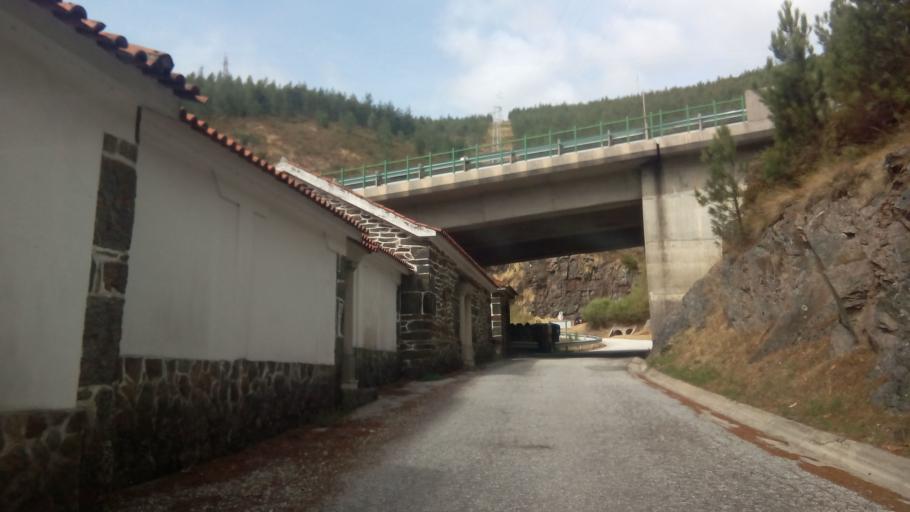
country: PT
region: Vila Real
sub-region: Mesao Frio
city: Mesao Frio
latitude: 41.2760
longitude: -7.9327
